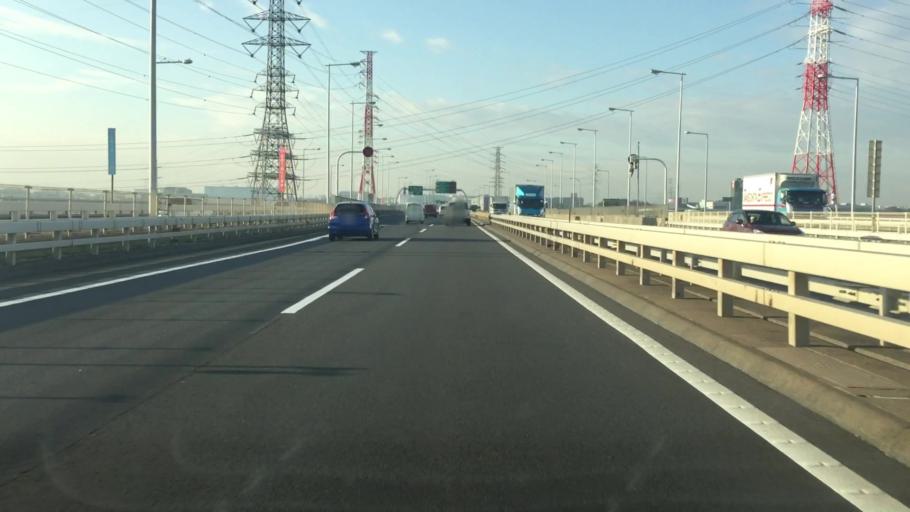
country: JP
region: Saitama
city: Wako
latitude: 35.8078
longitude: 139.6254
